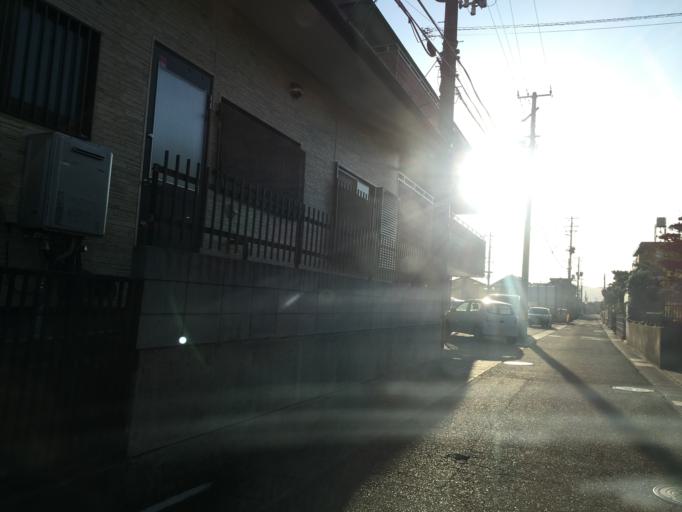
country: JP
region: Fukushima
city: Koriyama
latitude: 37.4003
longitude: 140.3513
